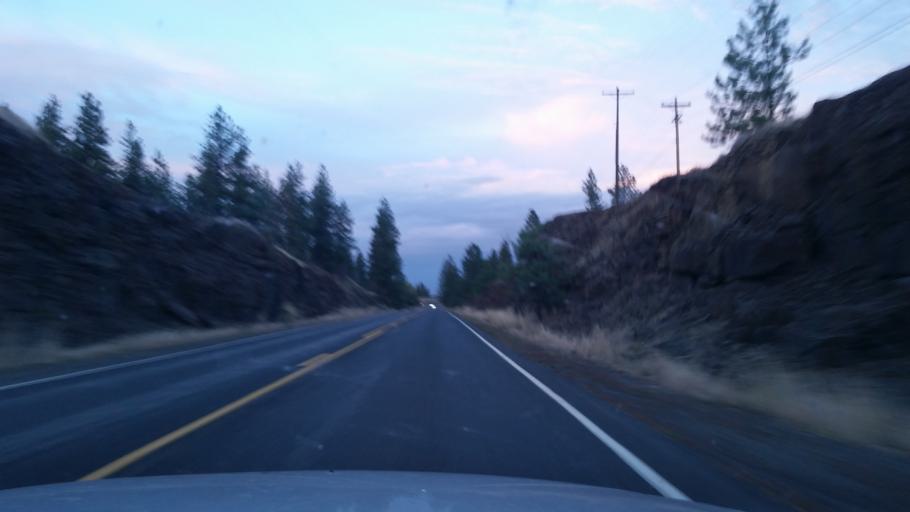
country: US
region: Washington
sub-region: Spokane County
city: Spokane
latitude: 47.6331
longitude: -117.4945
